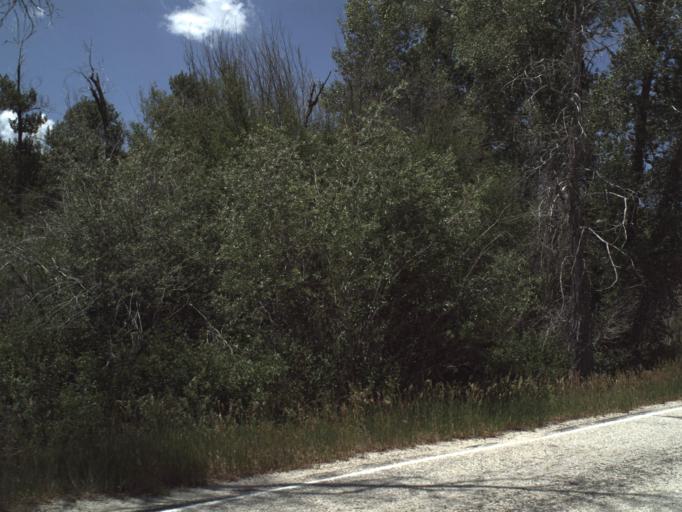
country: US
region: Utah
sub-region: Weber County
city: Wolf Creek
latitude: 41.3143
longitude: -111.6151
